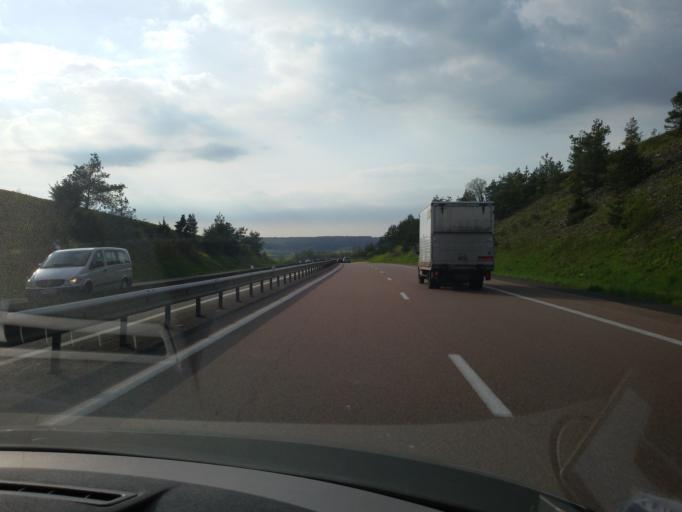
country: FR
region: Champagne-Ardenne
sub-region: Departement de l'Aube
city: Ville-sous-la-Ferte
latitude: 48.0977
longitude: 4.8178
